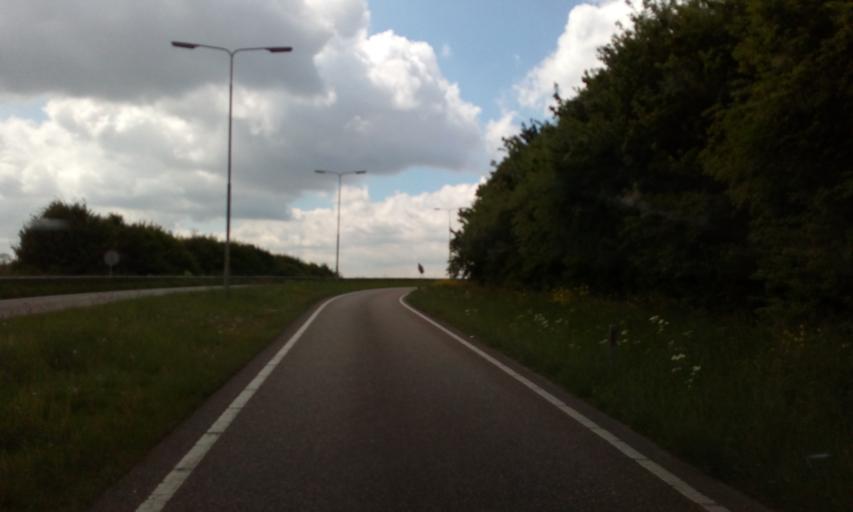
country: NL
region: South Holland
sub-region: Gemeente Hendrik-Ido-Ambacht
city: Hendrik-Ido-Ambacht
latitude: 51.8553
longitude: 4.6264
